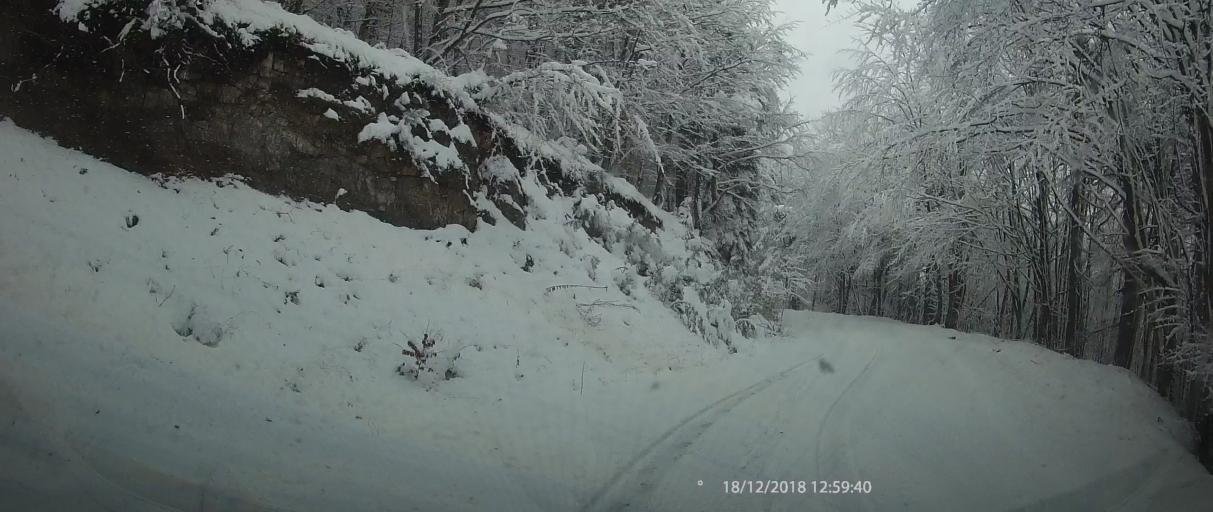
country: GR
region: Central Macedonia
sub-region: Nomos Pierias
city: Litochoro
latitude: 40.1085
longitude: 22.4616
